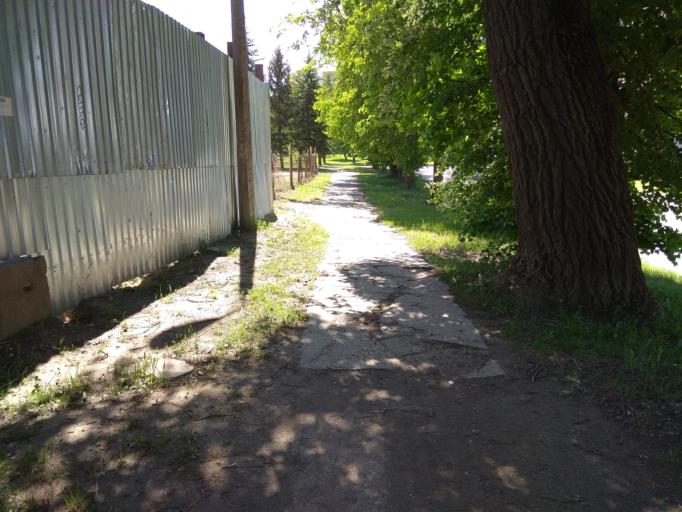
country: BY
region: Grodnenskaya
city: Hrodna
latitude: 53.7103
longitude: 23.8027
